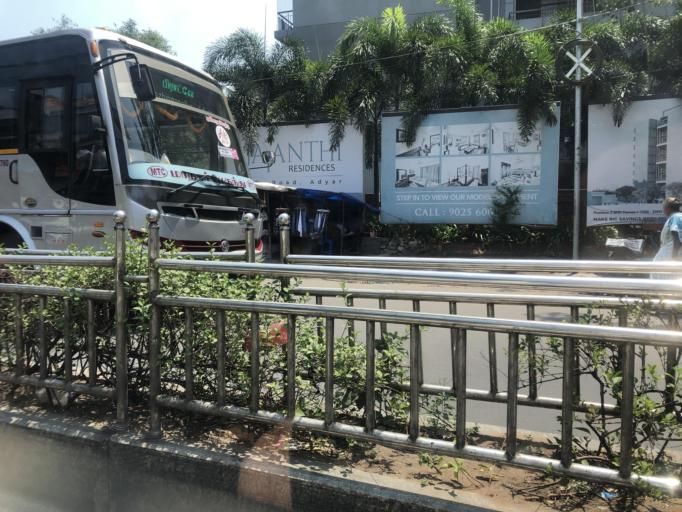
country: IN
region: Tamil Nadu
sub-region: Chennai
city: Gandhi Nagar
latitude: 12.9887
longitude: 80.2559
